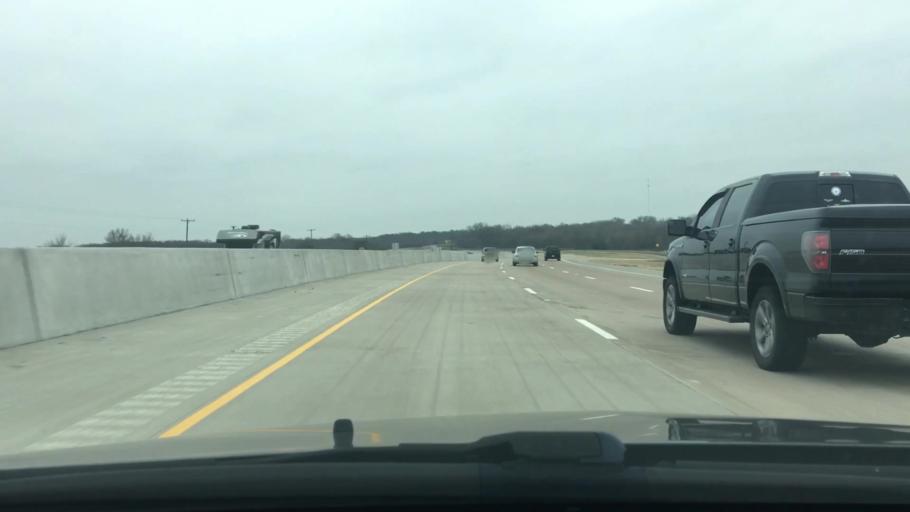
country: US
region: Texas
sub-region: Freestone County
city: Wortham
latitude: 31.9255
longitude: -96.4152
